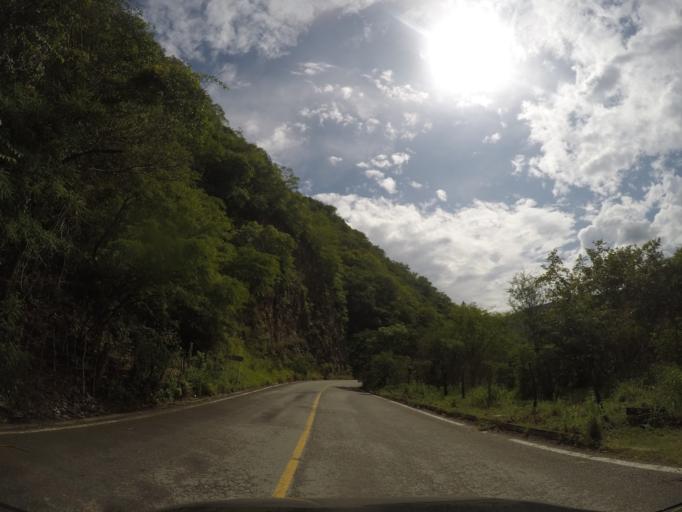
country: MX
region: Oaxaca
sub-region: San Jeronimo Coatlan
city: San Cristobal Honduras
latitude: 16.3706
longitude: -97.0845
